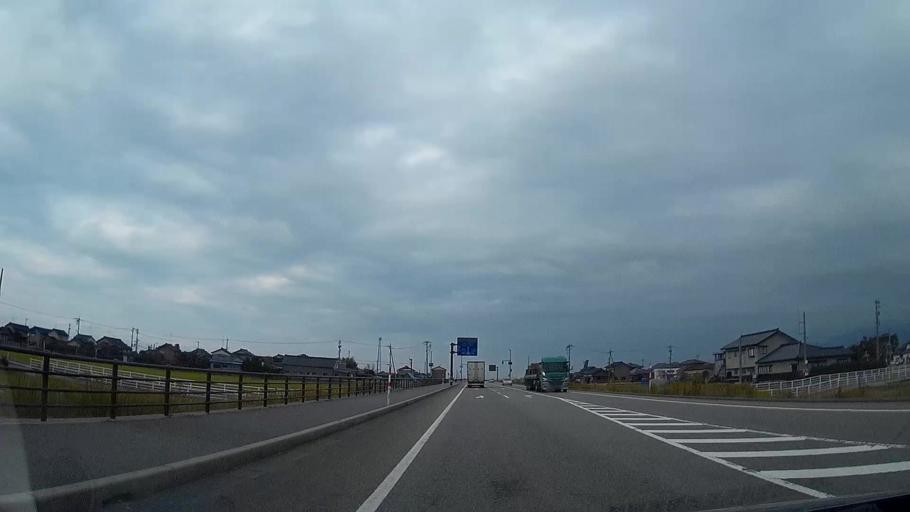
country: JP
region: Toyama
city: Nyuzen
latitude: 36.9197
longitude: 137.4655
